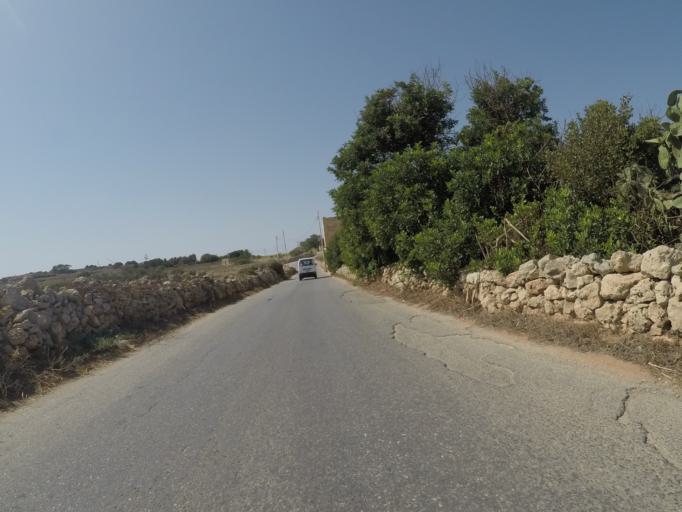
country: MT
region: L-Imgarr
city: Imgarr
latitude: 35.9260
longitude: 14.3783
